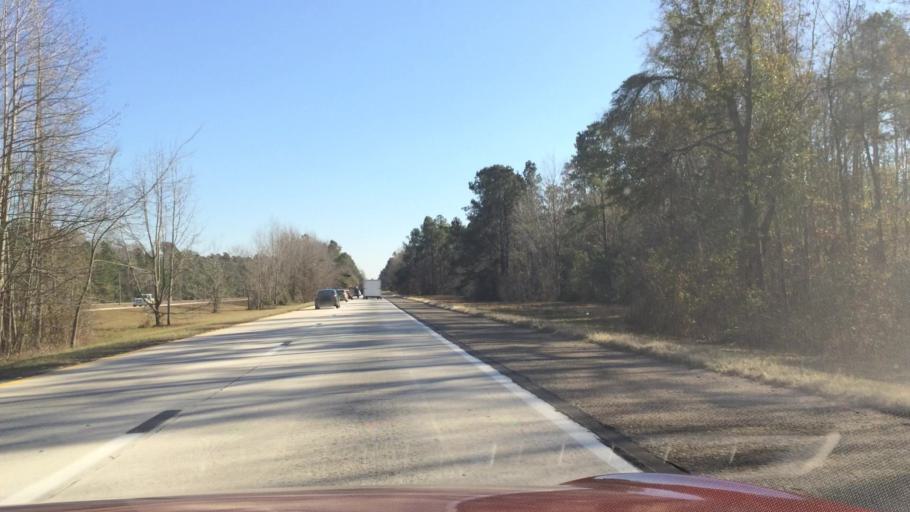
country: US
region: South Carolina
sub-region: Orangeburg County
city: Holly Hill
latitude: 33.2603
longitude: -80.4771
